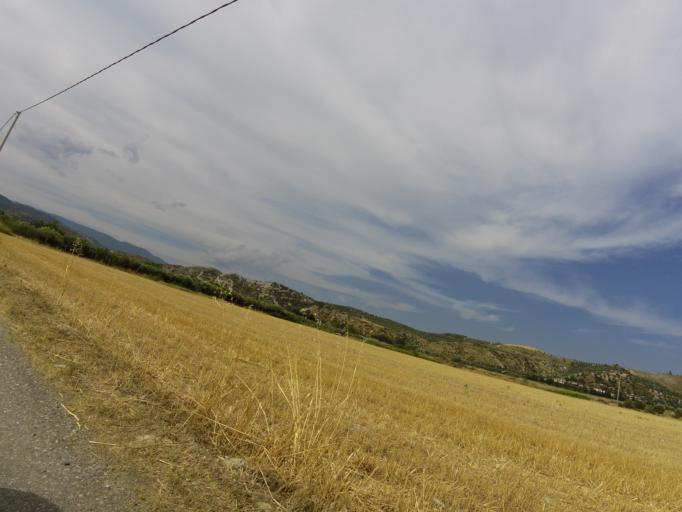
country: IT
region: Calabria
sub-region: Provincia di Reggio Calabria
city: Monasterace
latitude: 38.4526
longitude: 16.5184
